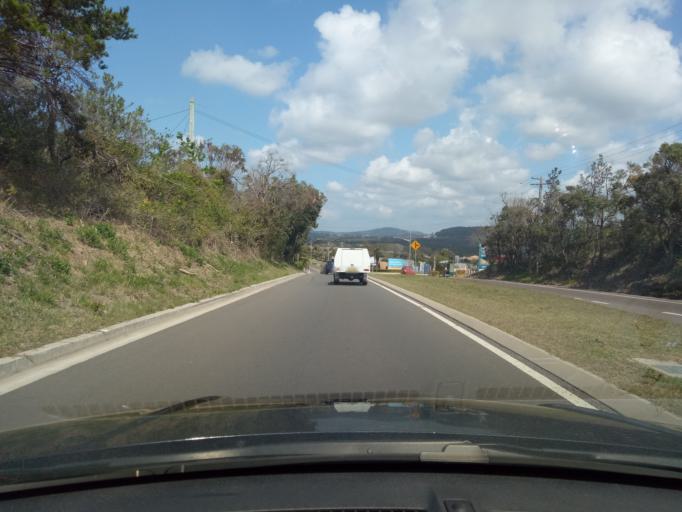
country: AU
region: New South Wales
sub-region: Gosford Shire
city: Forresters Beach
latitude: -33.4001
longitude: 151.4701
